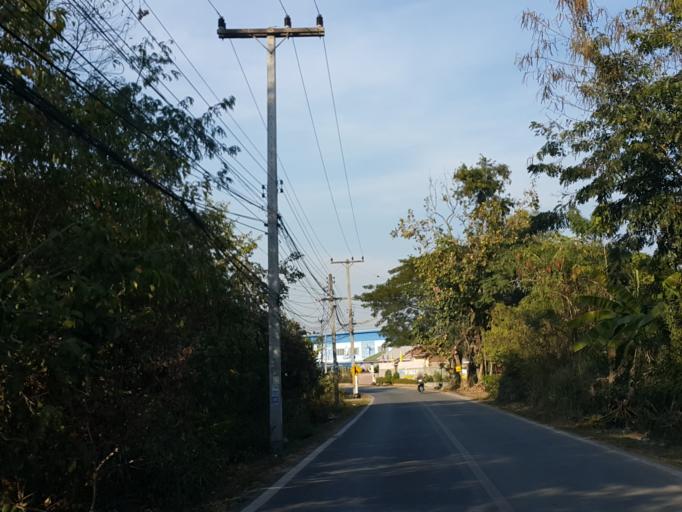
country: TH
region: Chiang Mai
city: San Sai
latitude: 18.7857
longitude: 99.0608
